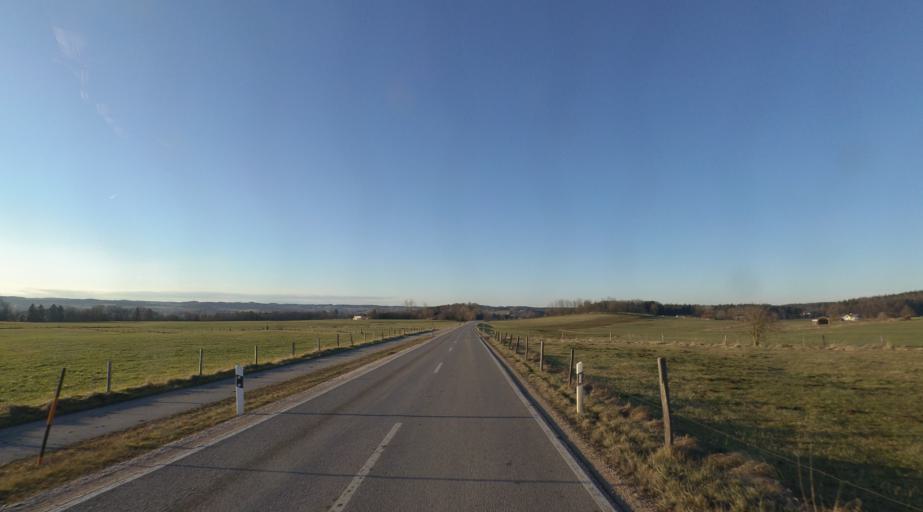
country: DE
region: Bavaria
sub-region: Upper Bavaria
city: Petting
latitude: 47.9428
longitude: 12.7986
